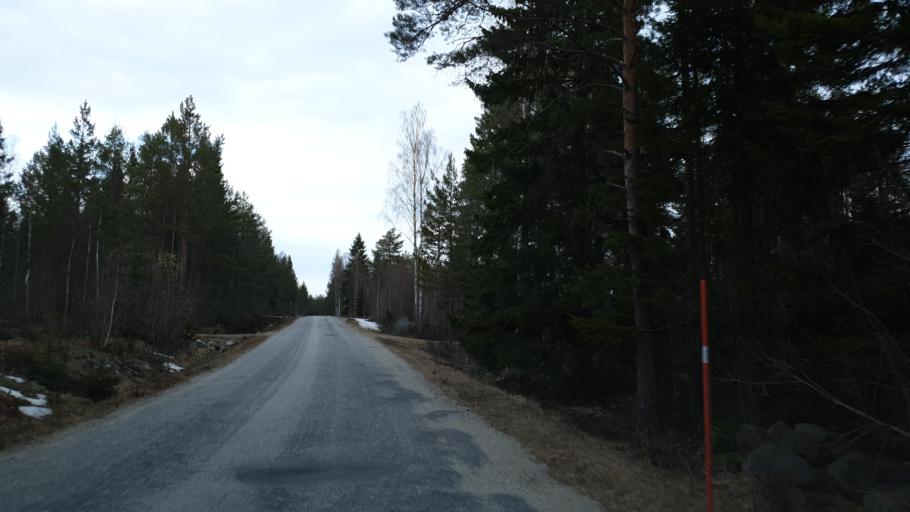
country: SE
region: Vaesternorrland
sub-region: Sundsvalls Kommun
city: Njurundabommen
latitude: 61.9698
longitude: 17.3822
